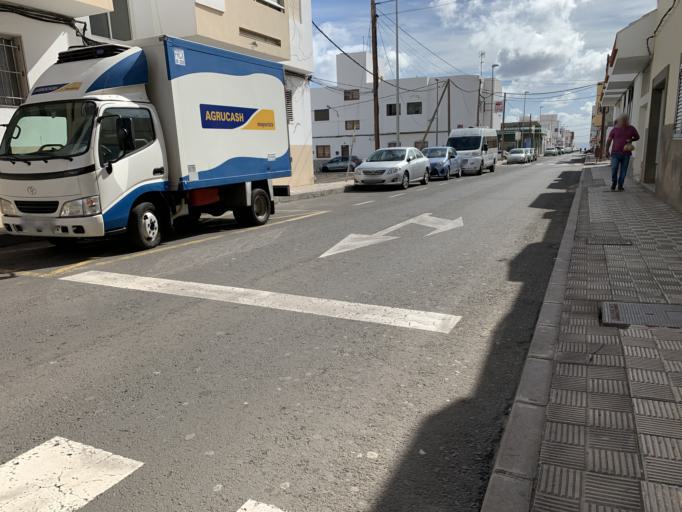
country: ES
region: Canary Islands
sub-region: Provincia de Las Palmas
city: Puerto del Rosario
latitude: 28.5051
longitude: -13.8498
